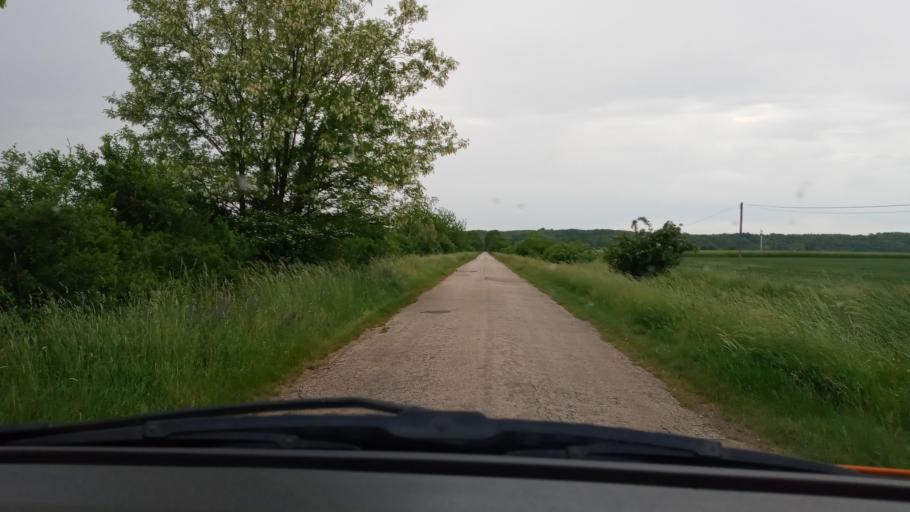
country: HU
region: Baranya
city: Harkany
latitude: 45.9083
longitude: 18.1391
